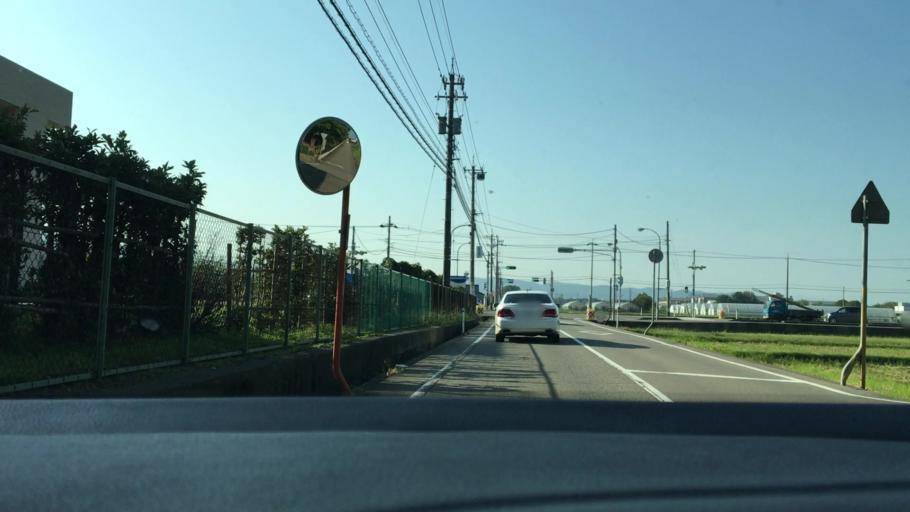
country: JP
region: Ishikawa
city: Nonoichi
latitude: 36.5152
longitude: 136.5997
